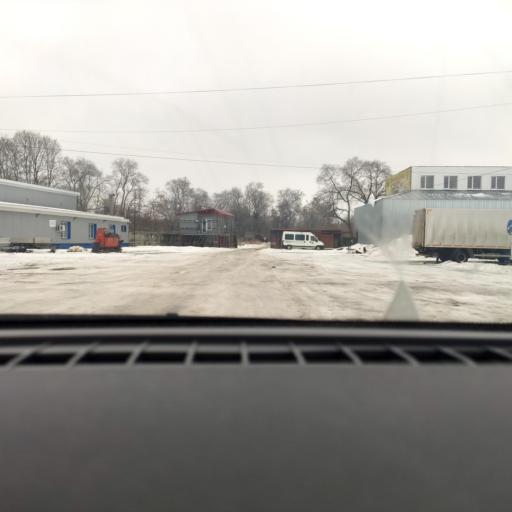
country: RU
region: Voronezj
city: Novaya Usman'
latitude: 51.6374
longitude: 39.3019
